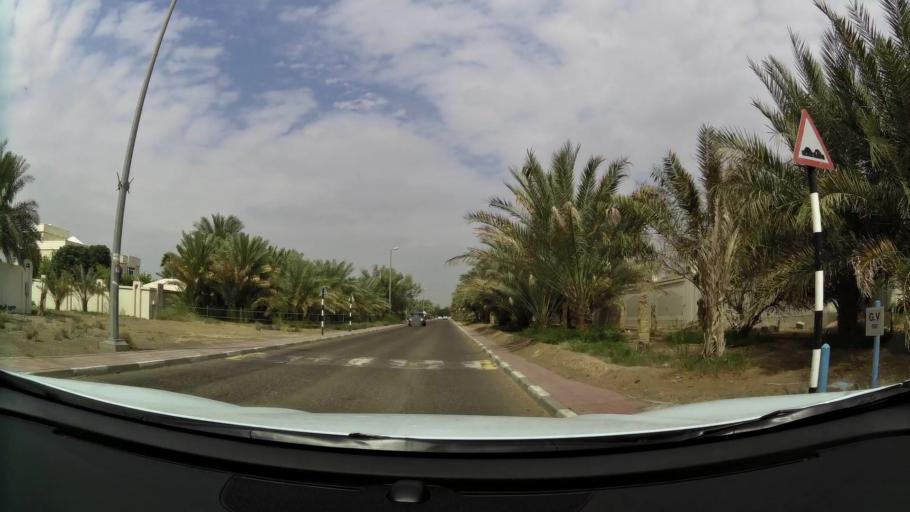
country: AE
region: Abu Dhabi
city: Al Ain
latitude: 24.2012
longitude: 55.8020
